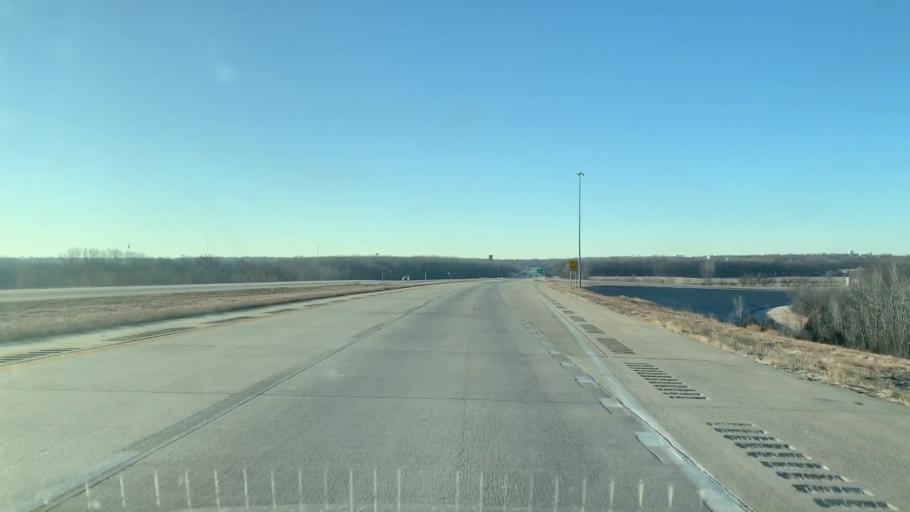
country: US
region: Kansas
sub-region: Bourbon County
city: Fort Scott
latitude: 37.8599
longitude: -94.7028
